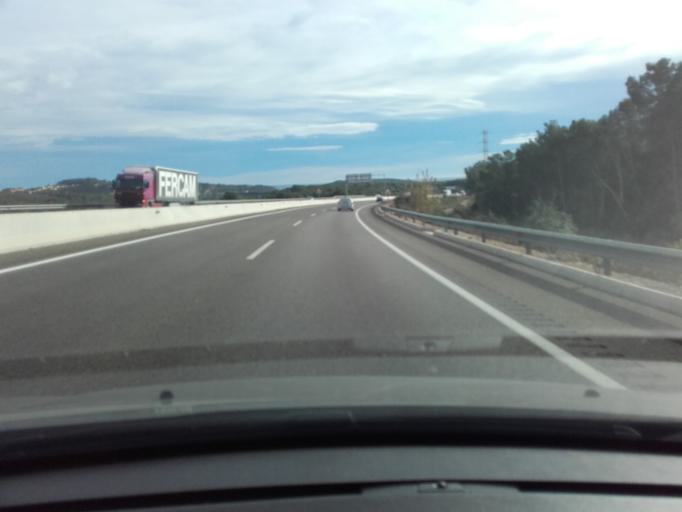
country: ES
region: Catalonia
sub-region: Provincia de Tarragona
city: el Catllar
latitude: 41.1434
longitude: 1.3224
